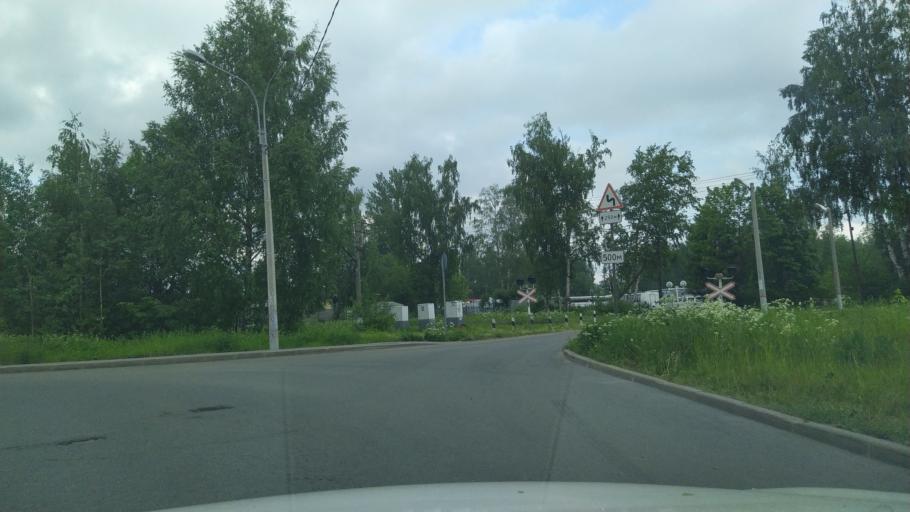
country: RU
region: St.-Petersburg
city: Krasnogvargeisky
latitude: 59.9836
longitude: 30.4414
